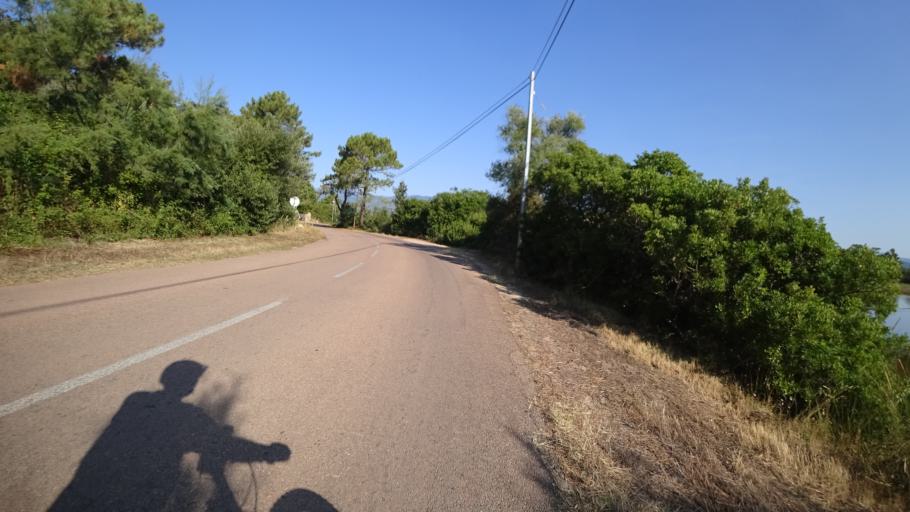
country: FR
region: Corsica
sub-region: Departement de la Corse-du-Sud
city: Porto-Vecchio
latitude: 41.6178
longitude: 9.3272
